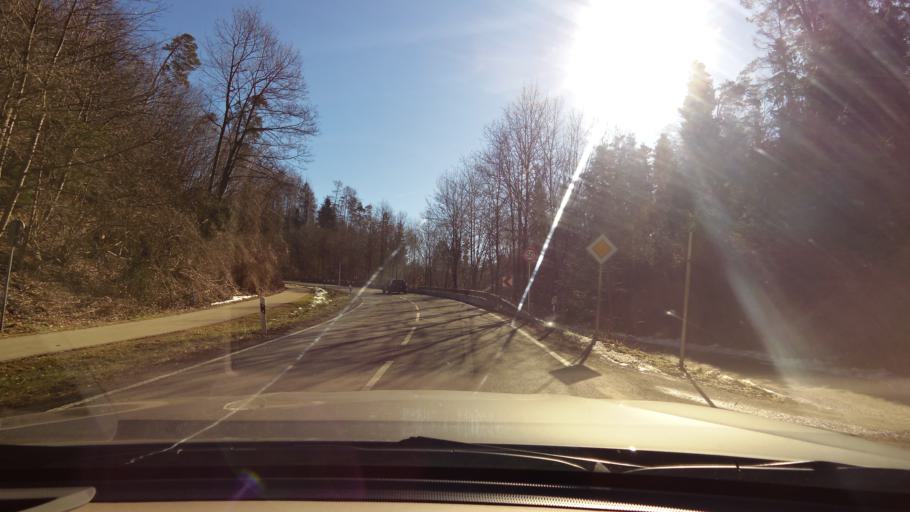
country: DE
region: Bavaria
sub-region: Upper Bavaria
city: Kraiburg am Inn
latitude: 48.1857
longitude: 12.4477
